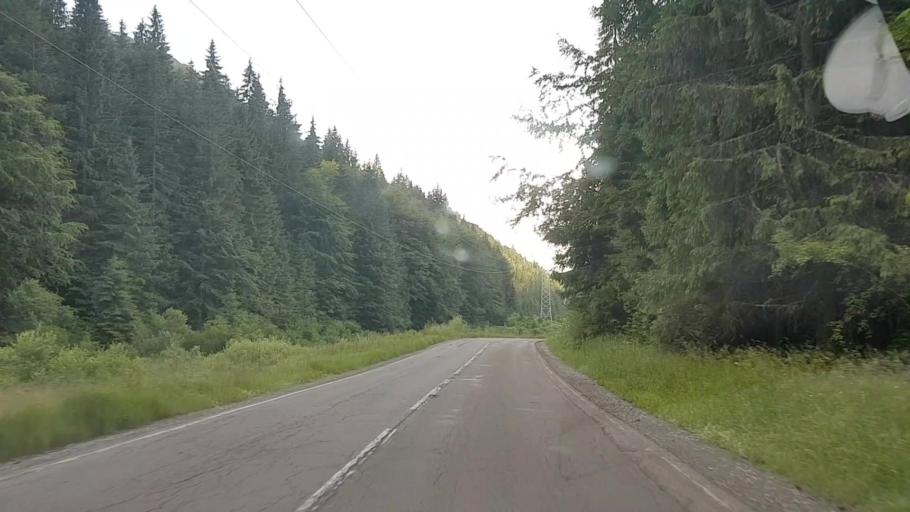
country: RO
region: Harghita
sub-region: Comuna Varsag
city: Varsag
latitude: 46.6313
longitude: 25.2640
